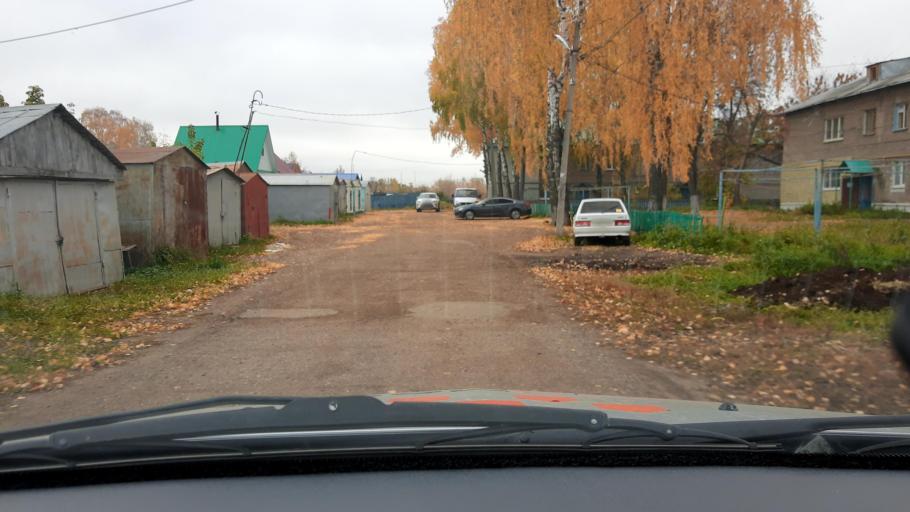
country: RU
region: Bashkortostan
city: Mikhaylovka
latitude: 54.8004
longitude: 55.8871
